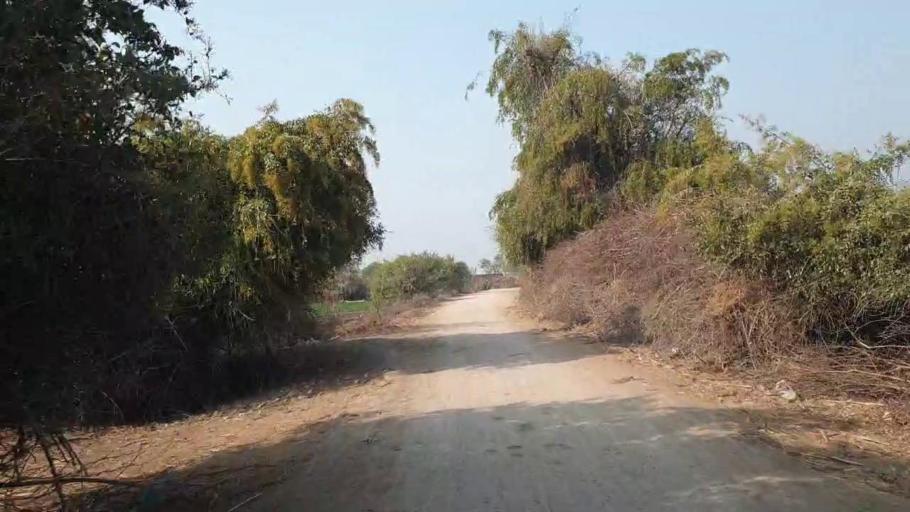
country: PK
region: Sindh
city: Bhit Shah
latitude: 25.8965
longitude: 68.4716
